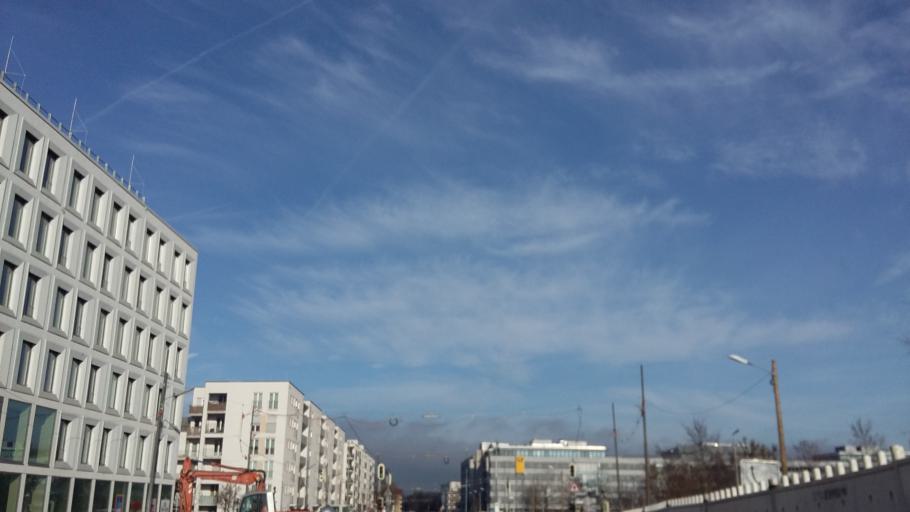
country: DE
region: Bavaria
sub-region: Upper Bavaria
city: Munich
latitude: 48.1458
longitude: 11.5203
